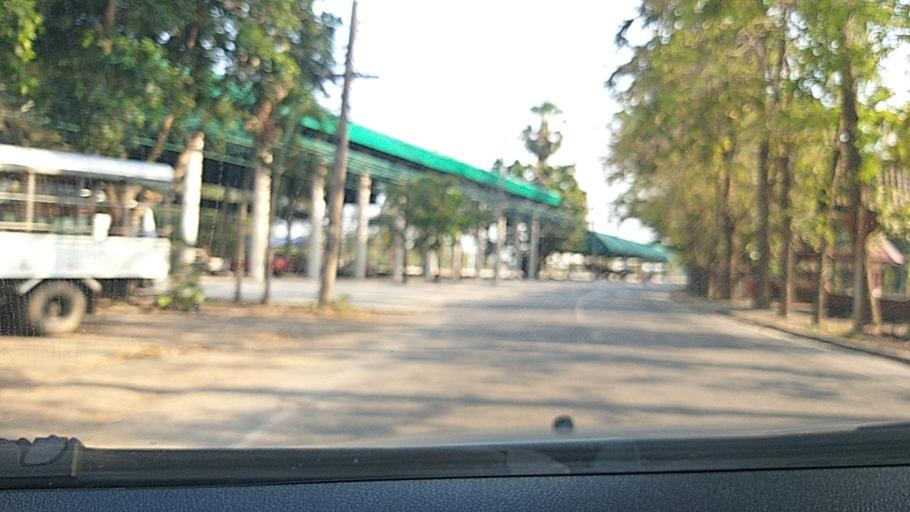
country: TH
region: Sing Buri
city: Sing Buri
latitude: 14.8514
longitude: 100.3901
